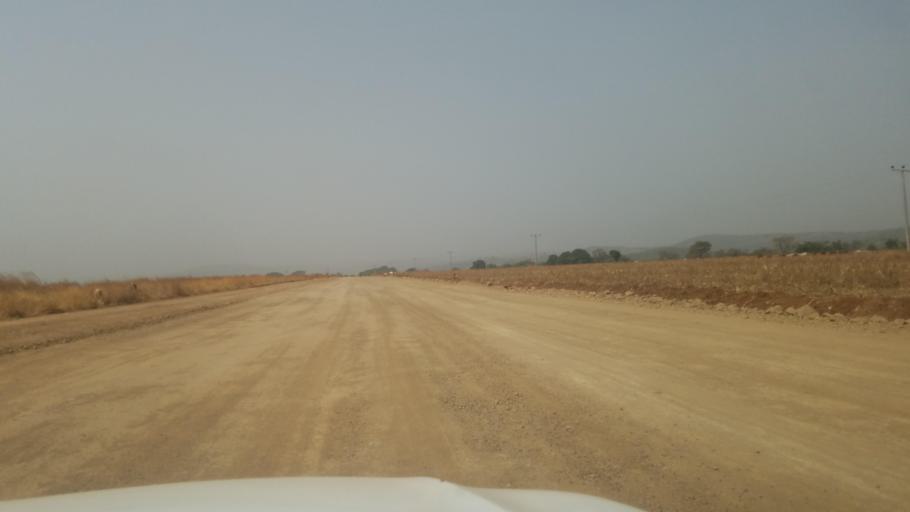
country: ET
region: Amhara
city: Bure
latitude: 10.8953
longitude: 36.4577
